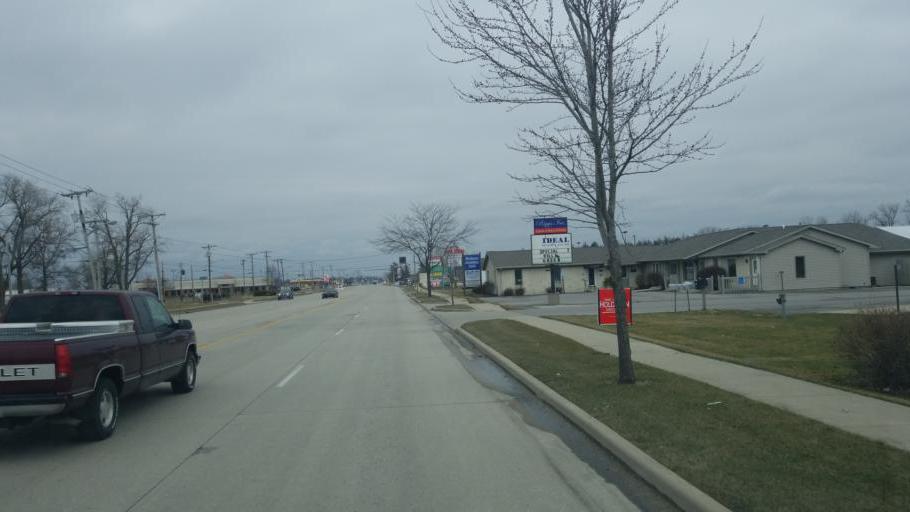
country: US
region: Indiana
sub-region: Adams County
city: Decatur
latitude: 40.8236
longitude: -84.9377
